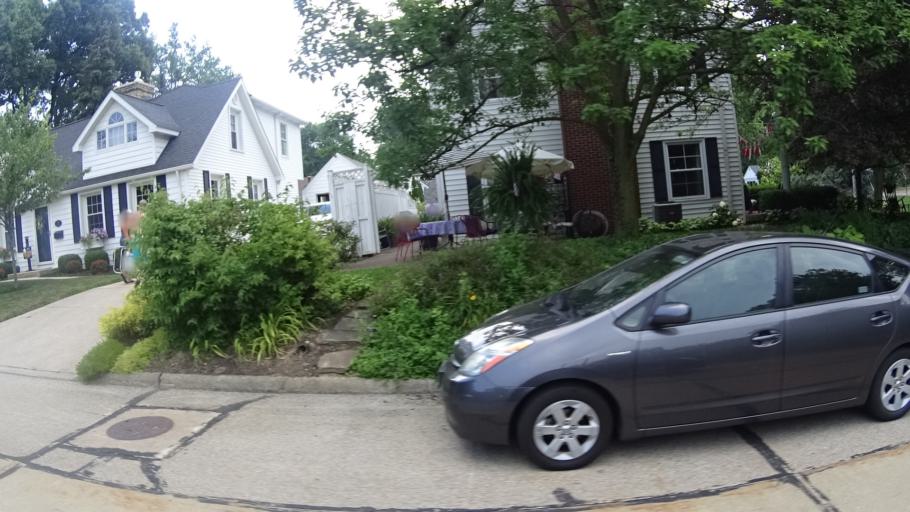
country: US
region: Ohio
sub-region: Erie County
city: Huron
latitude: 41.3897
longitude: -82.5363
